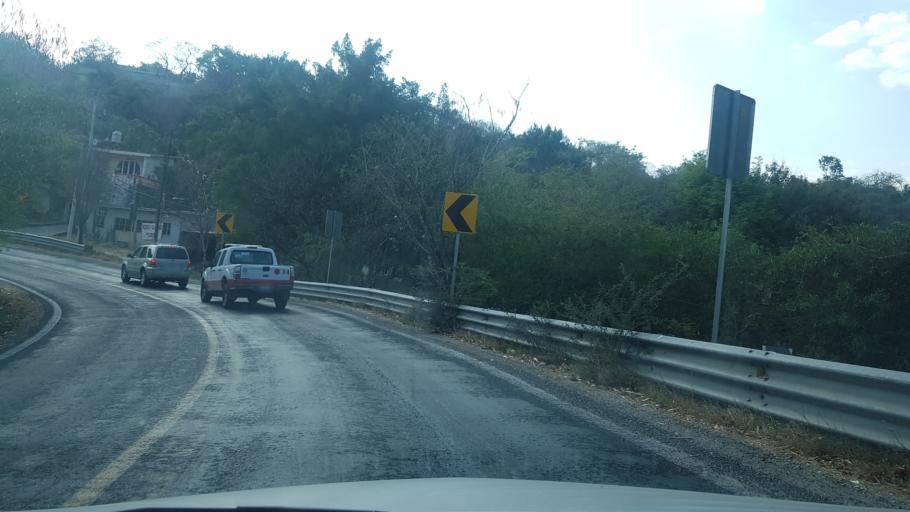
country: MX
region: Morelos
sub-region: Amacuzac
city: Amacuzac
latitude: 18.6048
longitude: -99.3678
